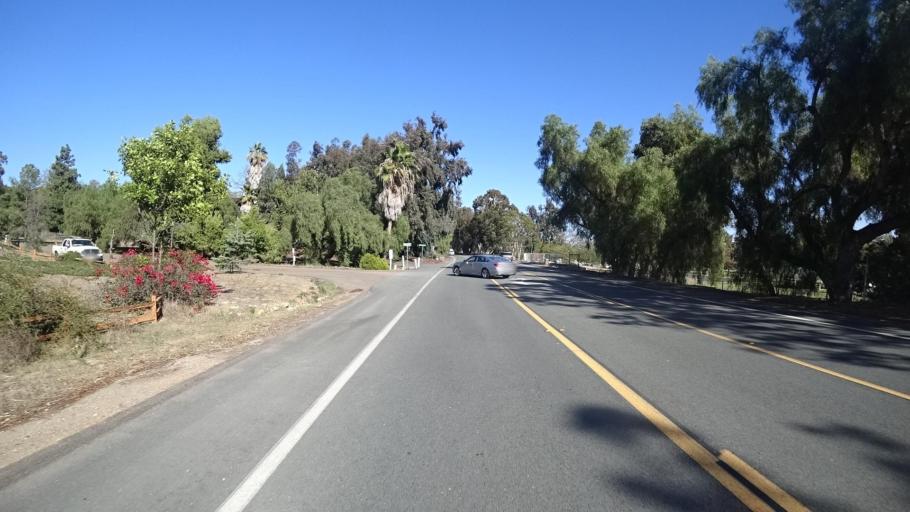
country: US
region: California
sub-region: San Diego County
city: Bonita
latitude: 32.6655
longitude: -117.0351
